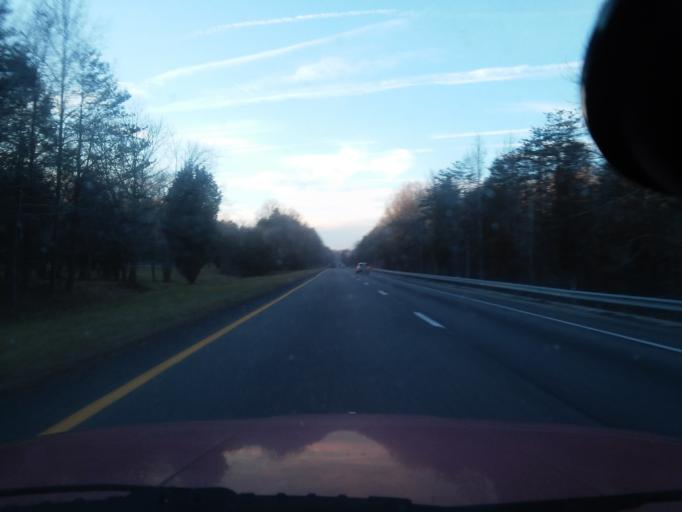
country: US
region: Virginia
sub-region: Goochland County
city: Goochland
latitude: 37.8104
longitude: -77.9337
